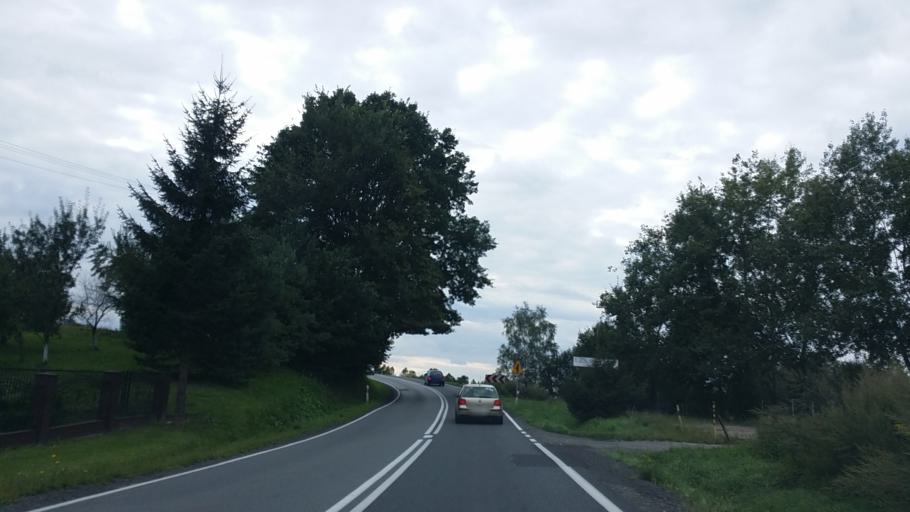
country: PL
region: Lesser Poland Voivodeship
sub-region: Powiat krakowski
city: Czernichow
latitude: 49.9609
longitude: 19.6585
